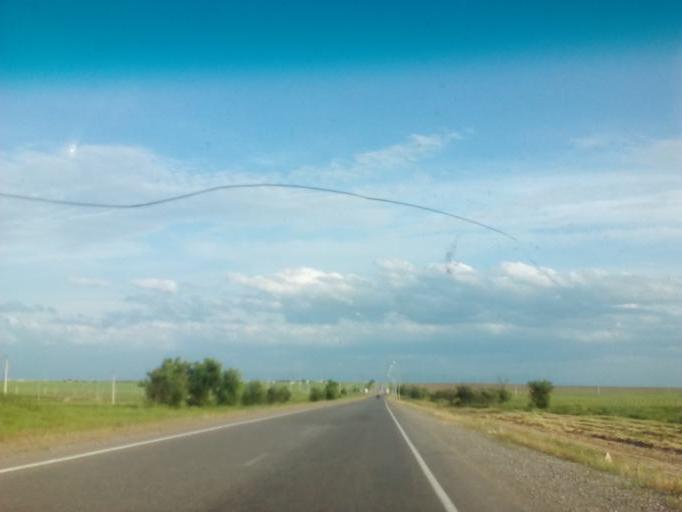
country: KZ
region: Ongtustik Qazaqstan
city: Temirlanovka
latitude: 42.5305
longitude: 69.3394
